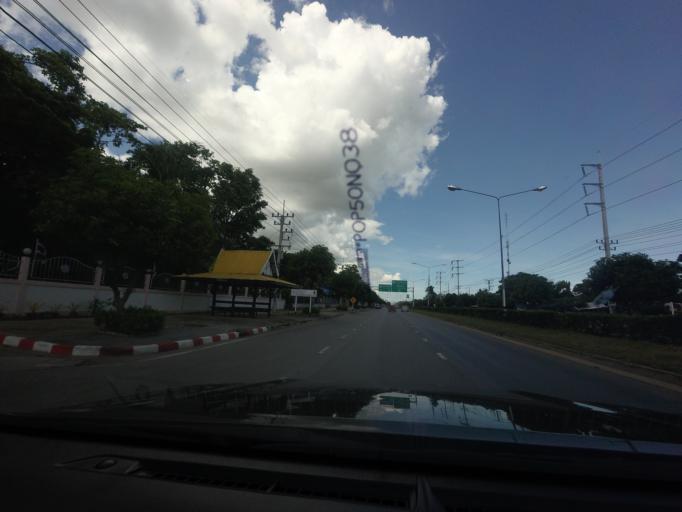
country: TH
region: Kanchanaburi
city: Phanom Thuan
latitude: 14.1259
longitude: 99.6913
